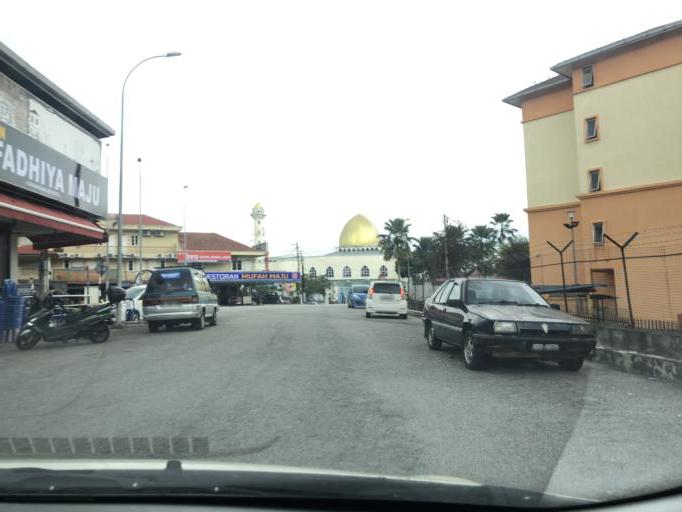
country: MY
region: Putrajaya
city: Putrajaya
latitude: 2.9253
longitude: 101.7597
